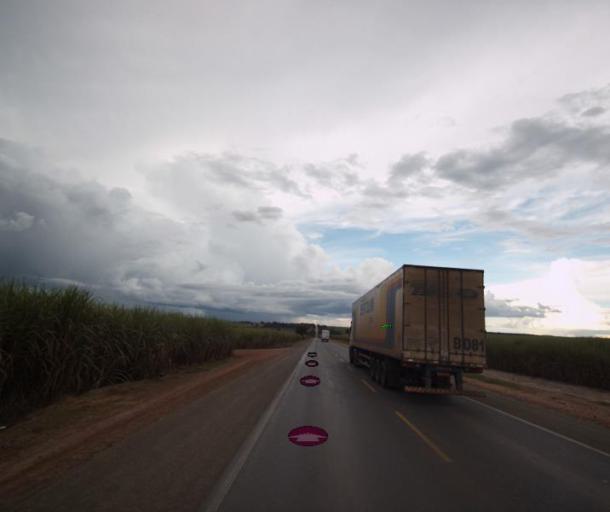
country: BR
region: Goias
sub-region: Itapaci
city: Itapaci
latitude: -14.9237
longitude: -49.3618
